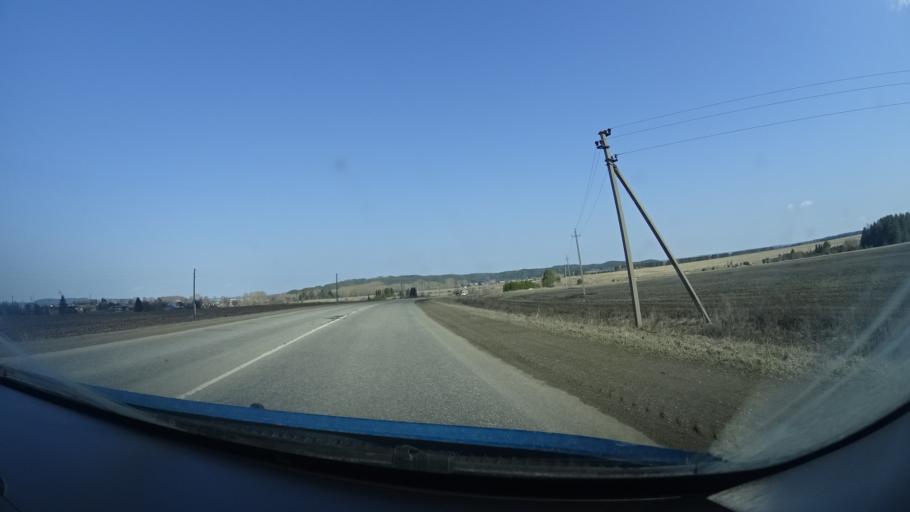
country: RU
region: Perm
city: Osa
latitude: 57.2825
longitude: 55.5661
